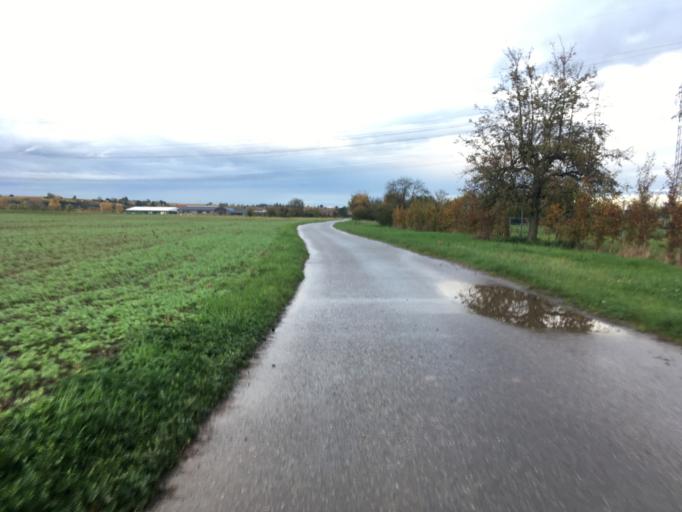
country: DE
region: Baden-Wuerttemberg
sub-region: Regierungsbezirk Stuttgart
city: Nordheim
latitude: 49.1062
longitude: 9.1607
